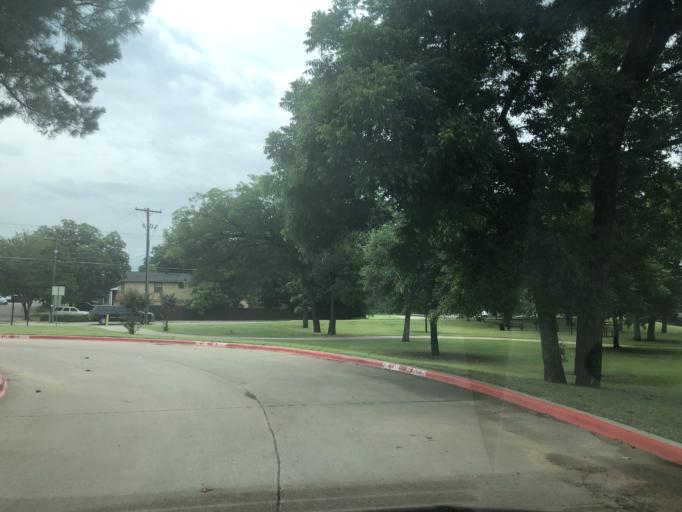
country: US
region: Texas
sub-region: Dallas County
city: Irving
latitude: 32.8040
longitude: -96.9475
